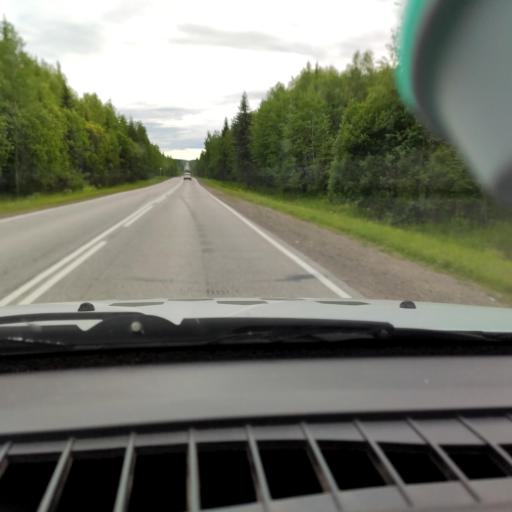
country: RU
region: Perm
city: Lys'va
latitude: 58.1237
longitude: 57.7181
